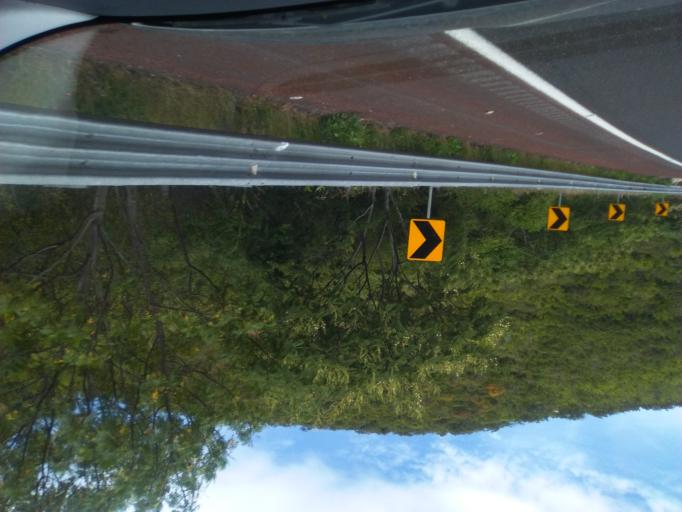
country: MX
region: Guerrero
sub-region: Eduardo Neri
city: Tlanipatla
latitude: 17.8496
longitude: -99.4052
